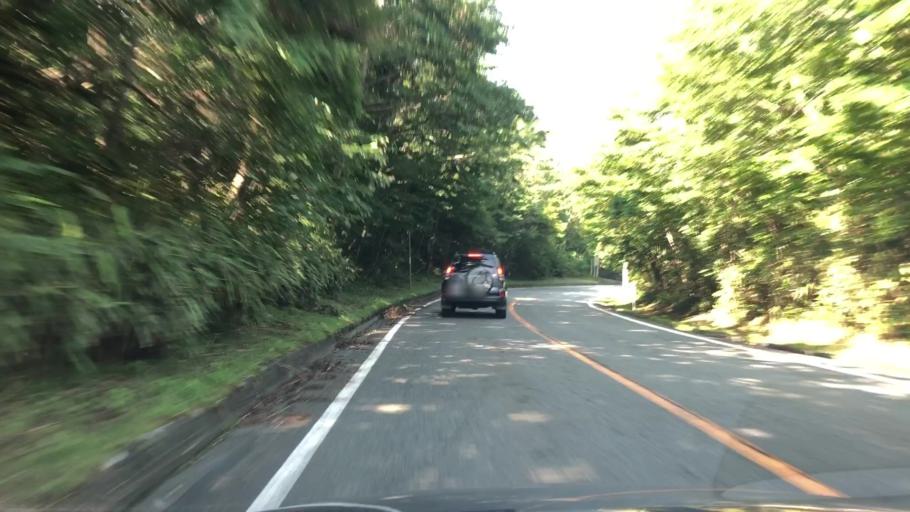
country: JP
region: Shizuoka
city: Gotemba
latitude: 35.3331
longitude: 138.8166
